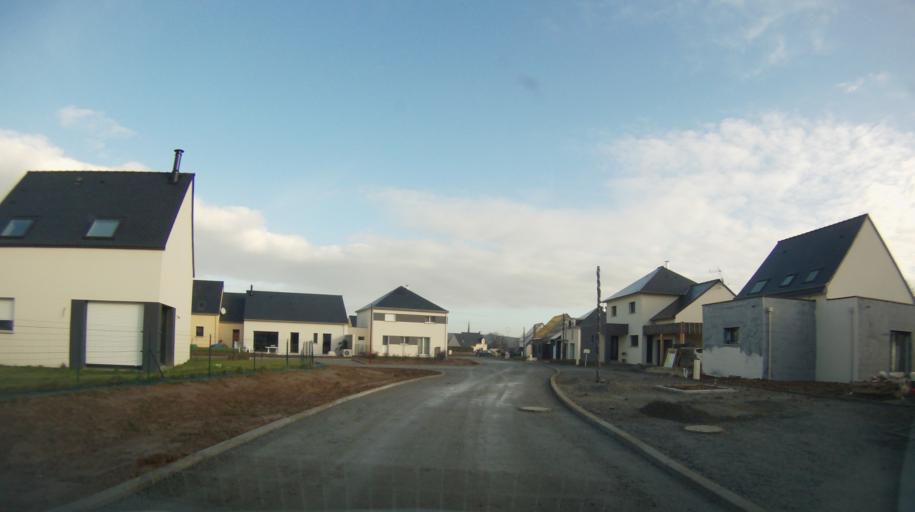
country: FR
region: Brittany
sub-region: Departement d'Ille-et-Vilaine
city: Janze
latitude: 47.9485
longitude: -1.5406
